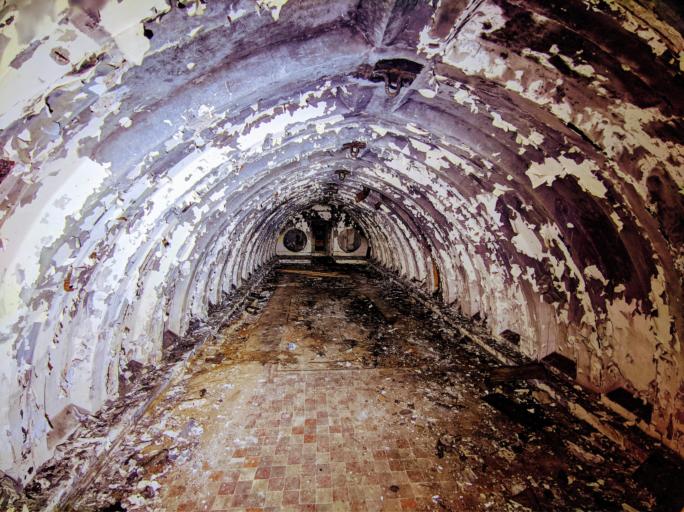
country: PL
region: Lower Silesian Voivodeship
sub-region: Powiat polkowicki
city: Przemkow
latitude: 51.4695
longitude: 15.8165
